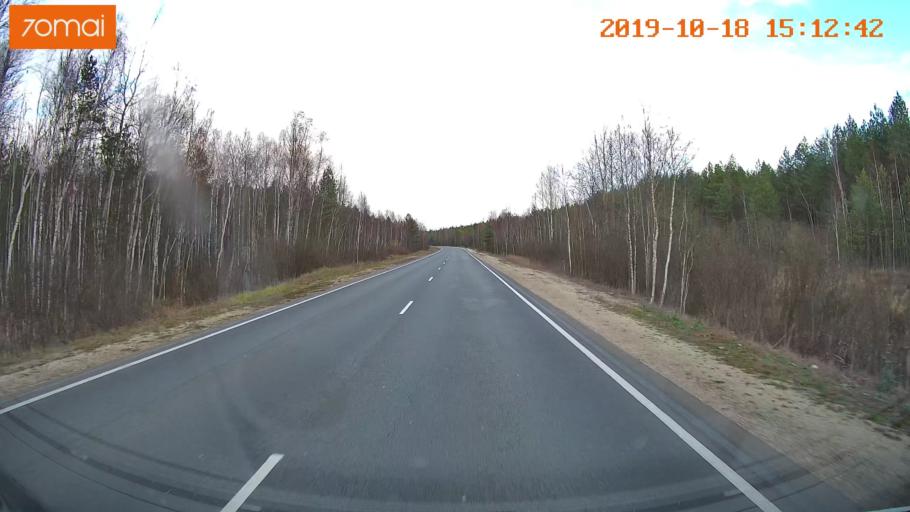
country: RU
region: Vladimir
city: Gus'-Khrustal'nyy
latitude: 55.5780
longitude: 40.7041
